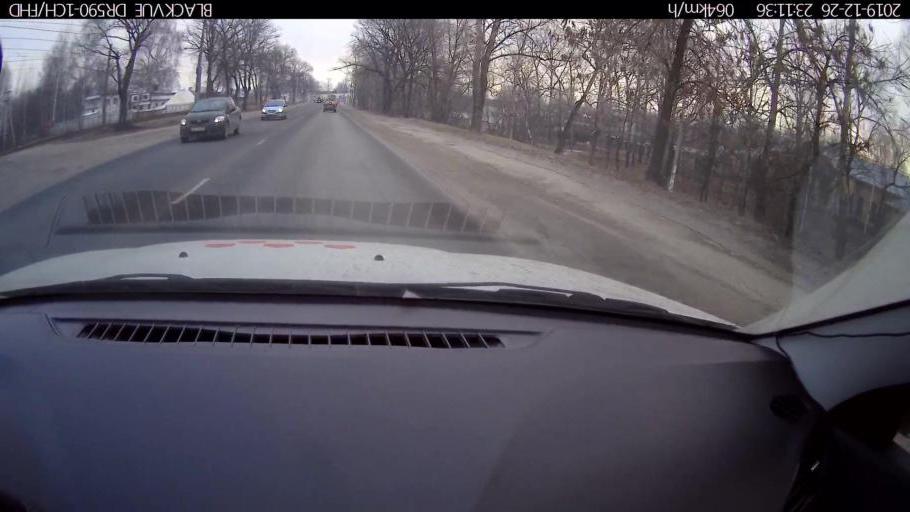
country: RU
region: Nizjnij Novgorod
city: Burevestnik
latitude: 56.2062
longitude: 43.8006
